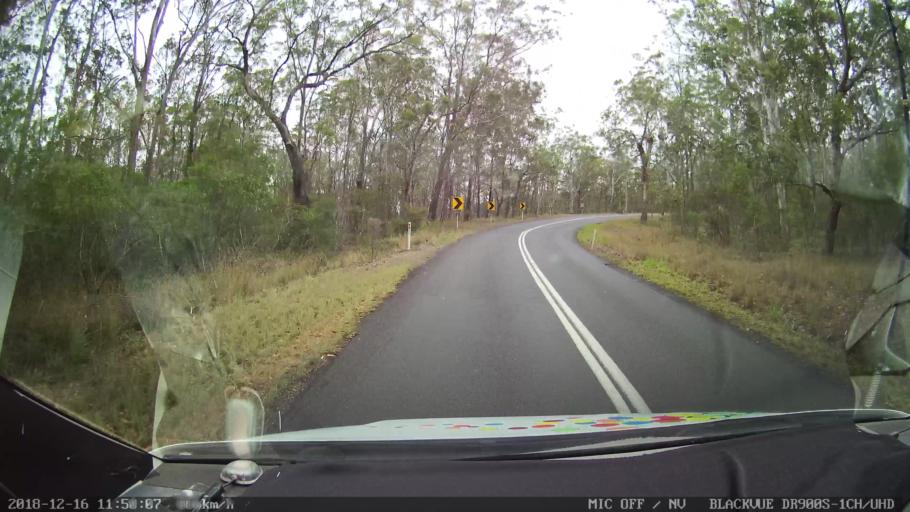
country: AU
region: New South Wales
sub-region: Tenterfield Municipality
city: Carrolls Creek
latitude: -28.9091
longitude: 152.2578
